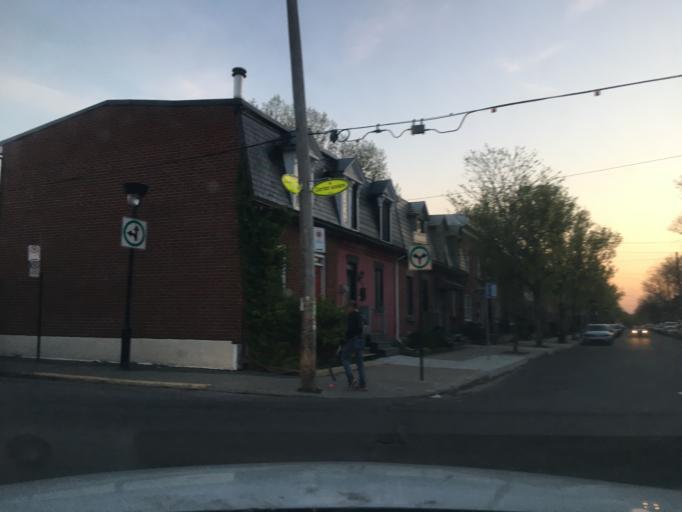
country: CA
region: Quebec
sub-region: Montreal
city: Montreal
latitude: 45.4806
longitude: -73.5530
